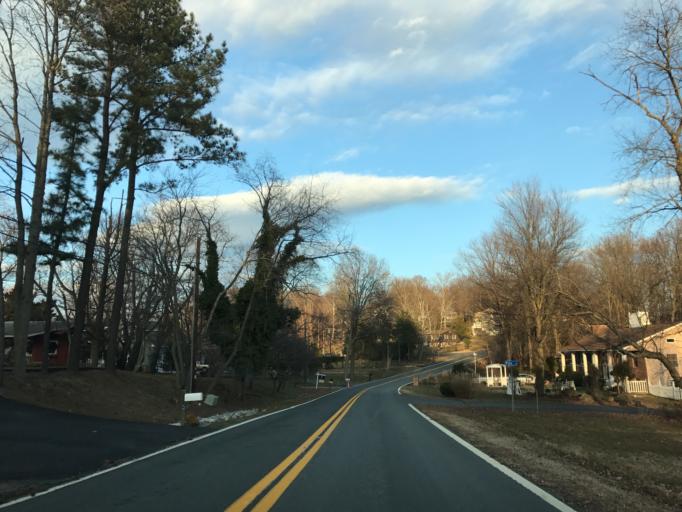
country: US
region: Maryland
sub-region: Cecil County
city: Charlestown
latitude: 39.4616
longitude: -76.0029
